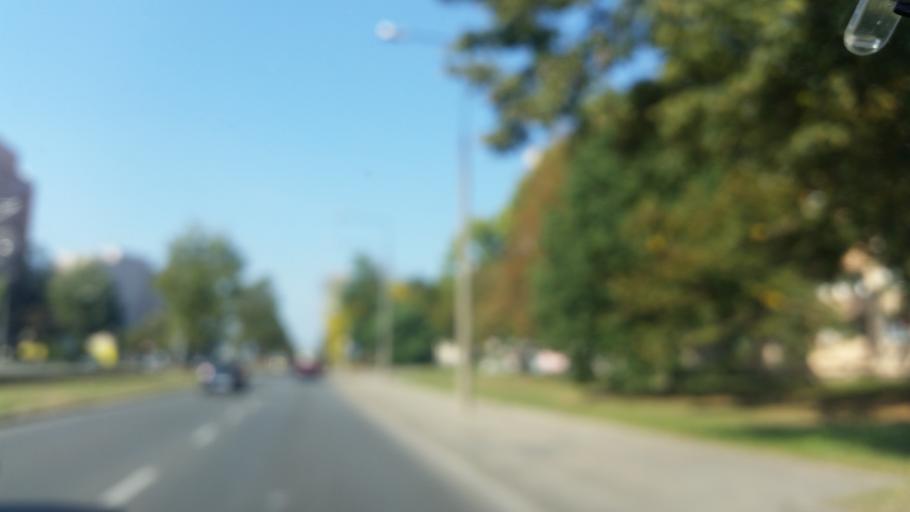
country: PL
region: Masovian Voivodeship
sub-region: Warszawa
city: Bemowo
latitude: 52.2231
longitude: 20.9172
